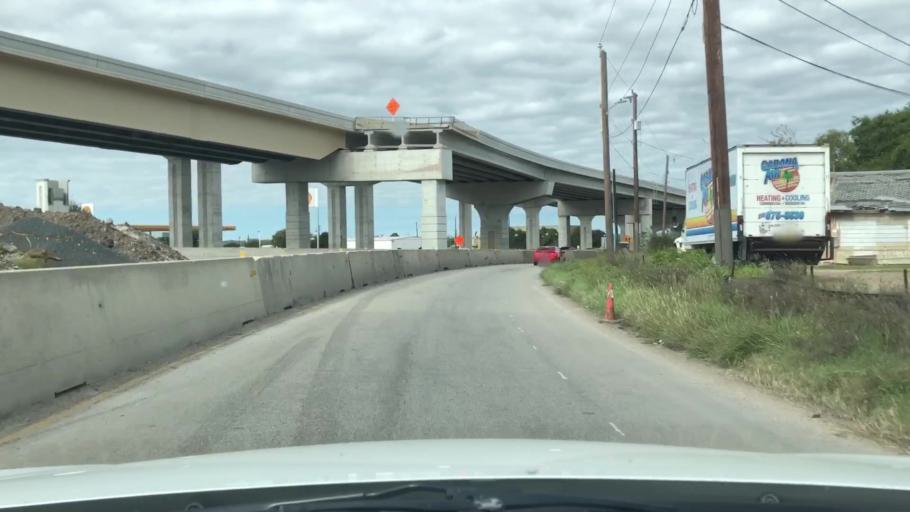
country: US
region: Texas
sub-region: Bexar County
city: Lackland Air Force Base
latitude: 29.3990
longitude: -98.6490
